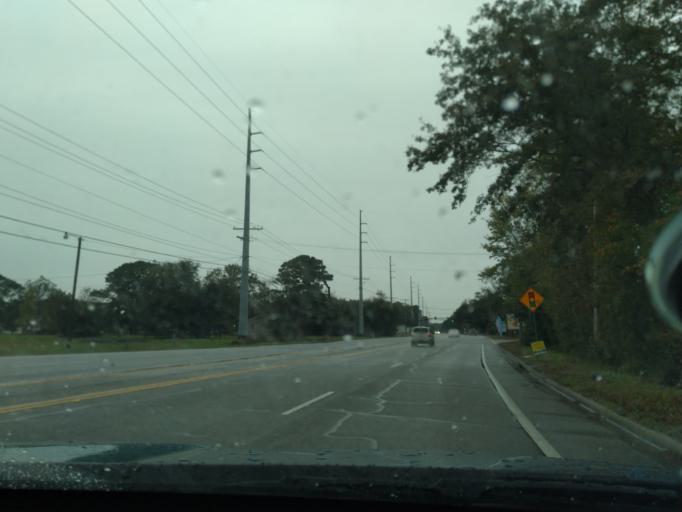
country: US
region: South Carolina
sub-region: Charleston County
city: Folly Beach
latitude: 32.6996
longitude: -79.9677
